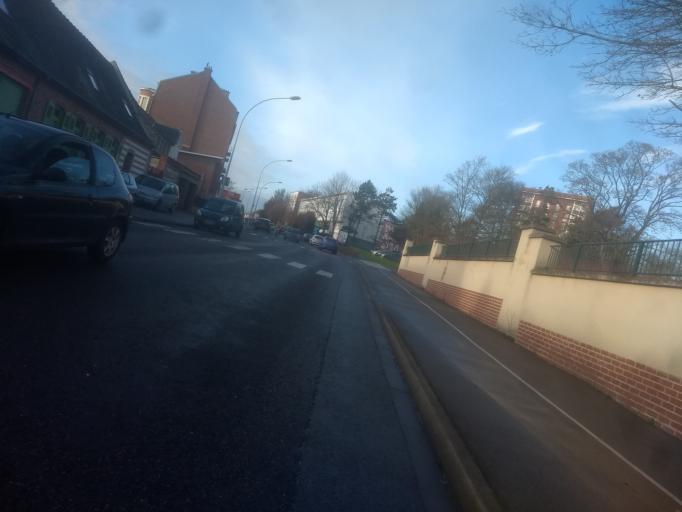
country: FR
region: Nord-Pas-de-Calais
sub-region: Departement du Pas-de-Calais
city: Sainte-Catherine
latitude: 50.2930
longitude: 2.7509
